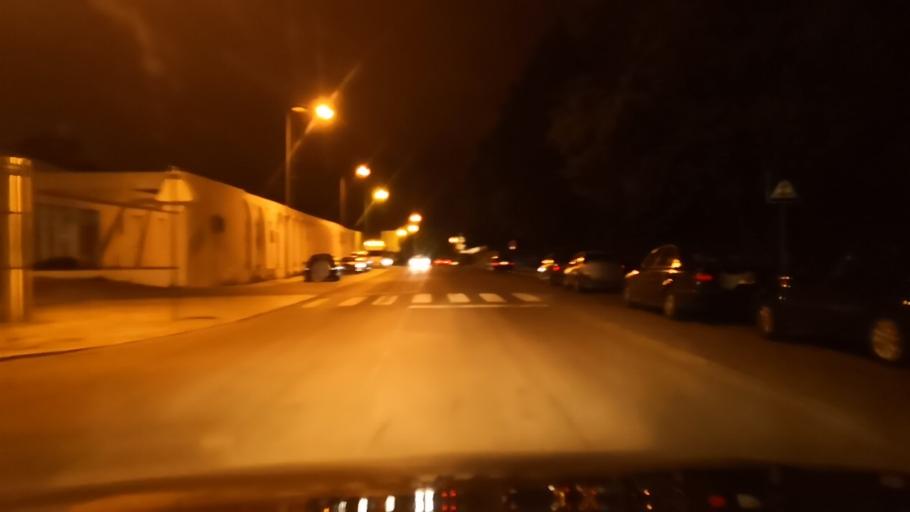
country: PT
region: Evora
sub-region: Estremoz
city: Estremoz
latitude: 38.8491
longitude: -7.5859
